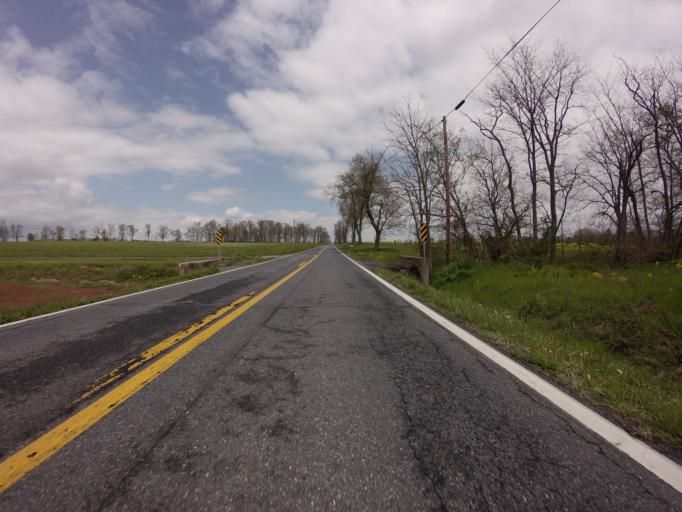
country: US
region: Maryland
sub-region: Frederick County
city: Thurmont
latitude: 39.5849
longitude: -77.3634
